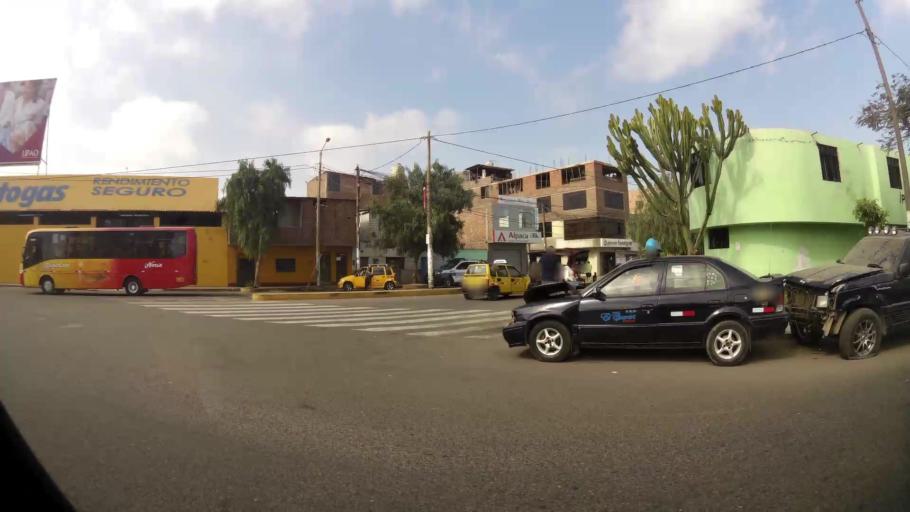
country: PE
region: La Libertad
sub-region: Provincia de Trujillo
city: El Porvenir
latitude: -8.1033
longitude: -79.0107
